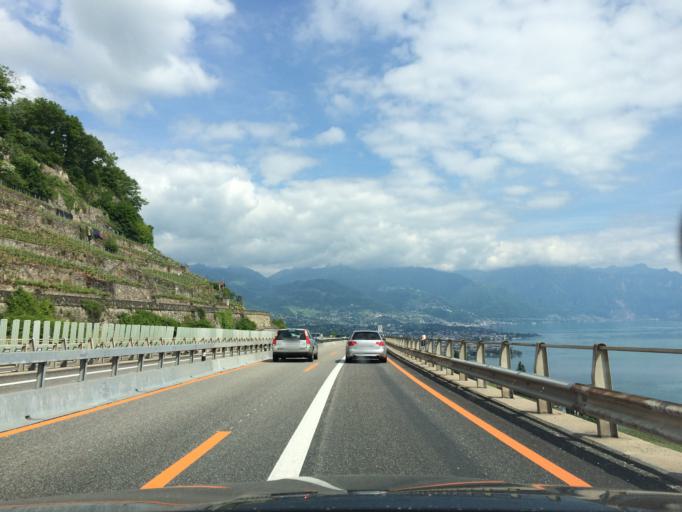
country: CH
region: Vaud
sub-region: Riviera-Pays-d'Enhaut District
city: Chardonne
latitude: 46.4761
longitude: 6.8028
